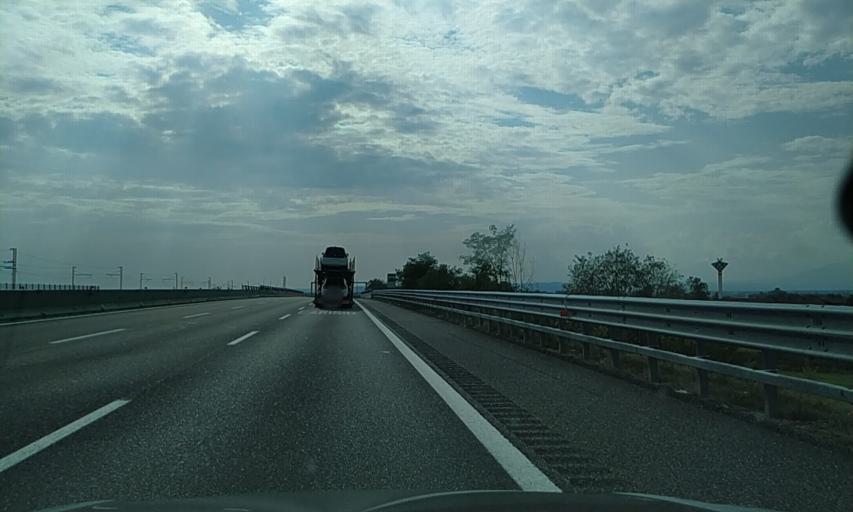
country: IT
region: Piedmont
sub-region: Provincia di Vercelli
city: Balocco
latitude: 45.4401
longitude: 8.2440
